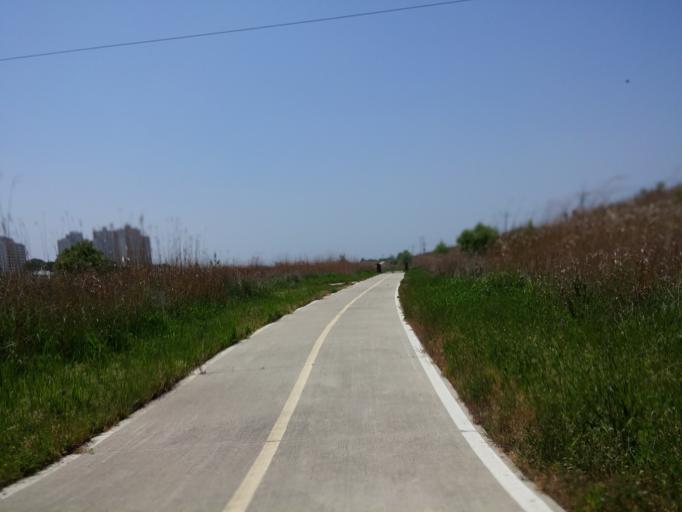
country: KR
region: Chungcheongnam-do
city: Nonsan
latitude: 36.2157
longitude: 127.0973
